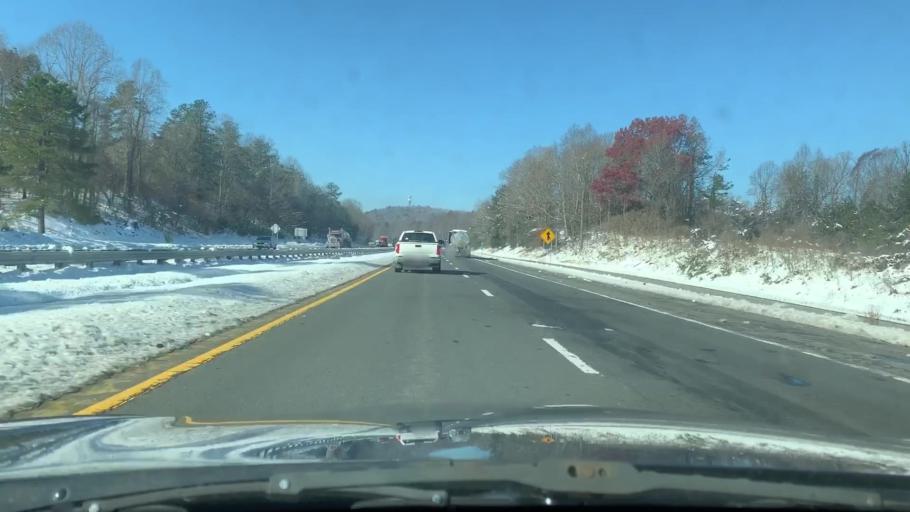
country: US
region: North Carolina
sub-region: Orange County
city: Hillsborough
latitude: 36.0574
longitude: -79.1050
